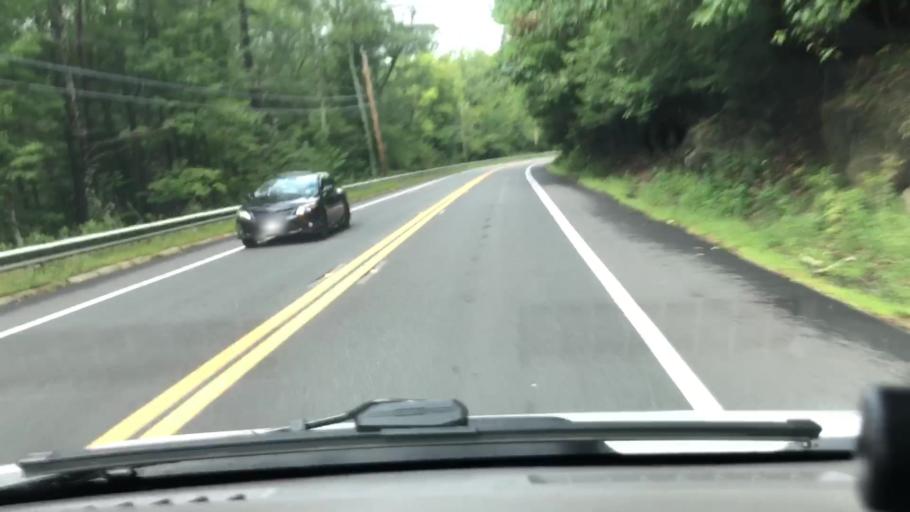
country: US
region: Massachusetts
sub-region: Franklin County
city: Ashfield
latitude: 42.5548
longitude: -72.8047
